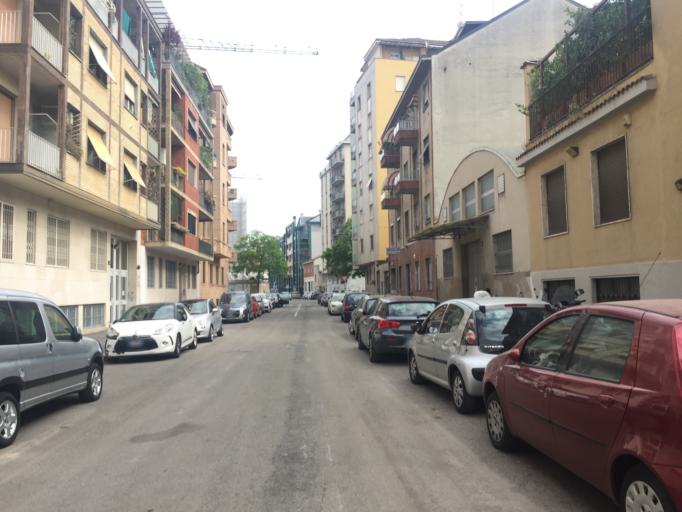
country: IT
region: Lombardy
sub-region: Citta metropolitana di Milano
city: Milano
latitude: 45.4938
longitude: 9.1638
